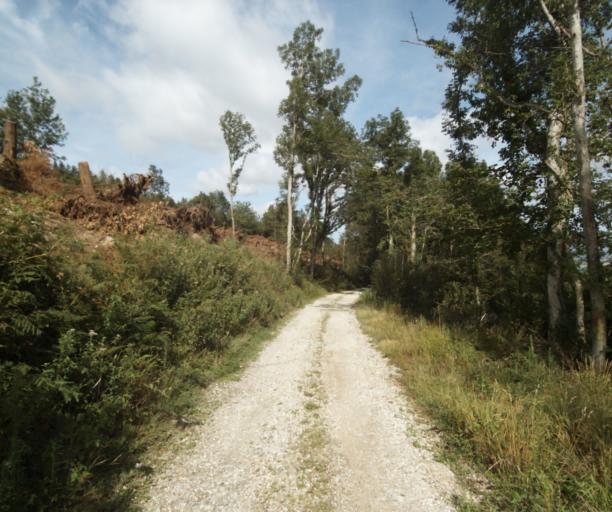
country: FR
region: Midi-Pyrenees
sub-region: Departement du Tarn
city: Dourgne
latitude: 43.4587
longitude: 2.1189
